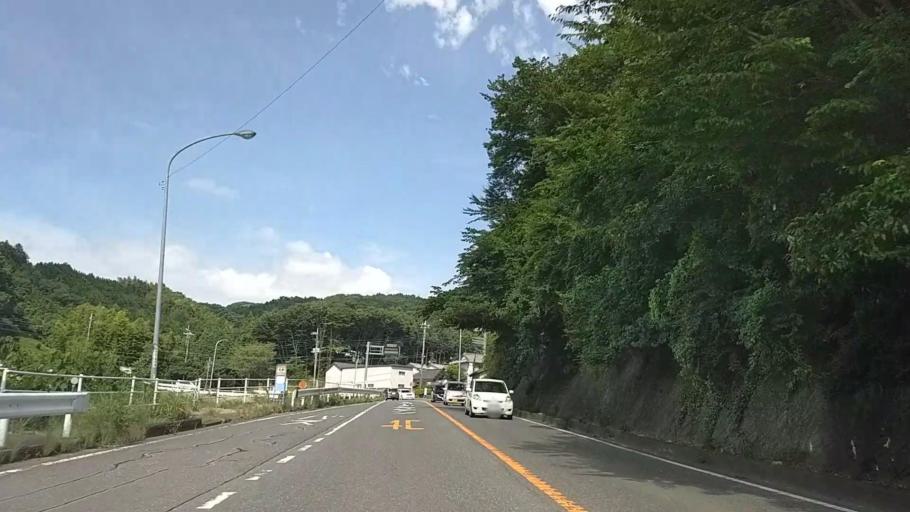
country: JP
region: Kanagawa
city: Hakone
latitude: 35.1458
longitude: 138.9805
